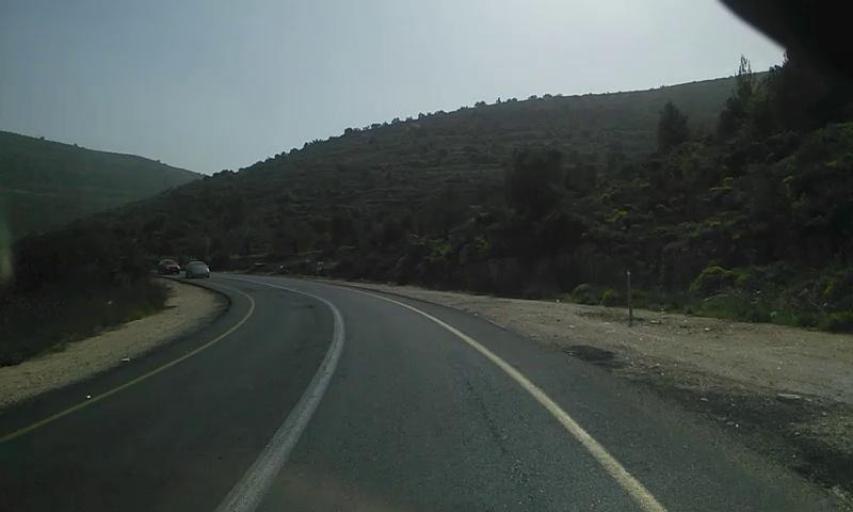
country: PS
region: West Bank
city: `Atarah
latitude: 31.9995
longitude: 35.2347
